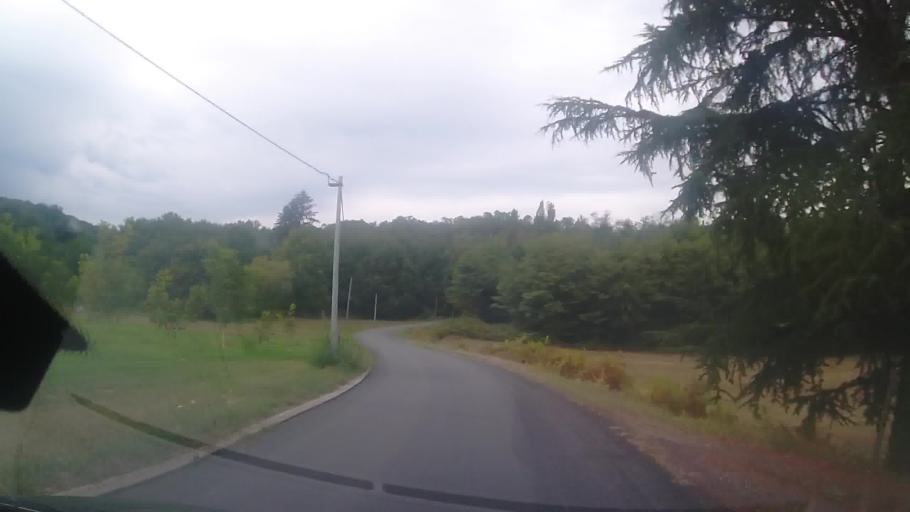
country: FR
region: Aquitaine
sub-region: Departement de la Dordogne
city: Eyvigues-et-Eybenes
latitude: 44.8386
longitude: 1.3611
